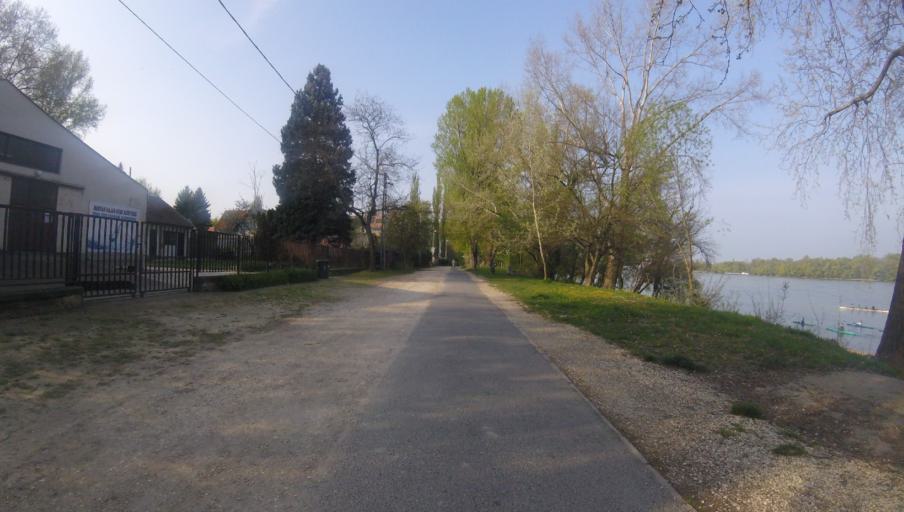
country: HU
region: Budapest
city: Budapest IV. keruelet
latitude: 47.5785
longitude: 19.0662
